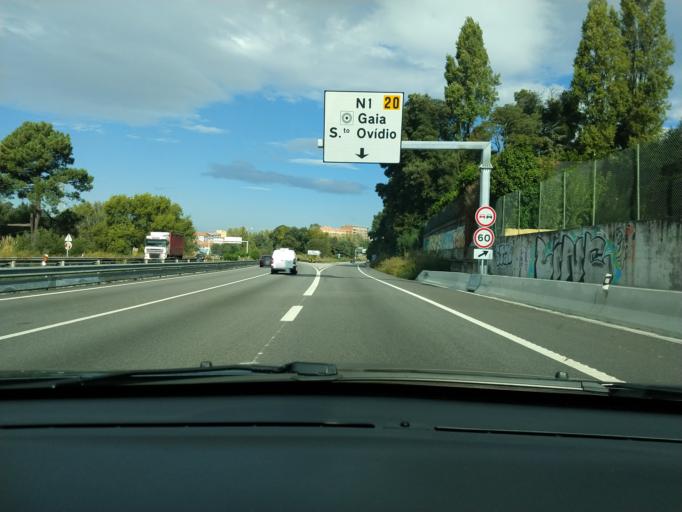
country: PT
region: Porto
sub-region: Vila Nova de Gaia
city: Vilar de Andorinho
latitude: 41.1079
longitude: -8.6047
